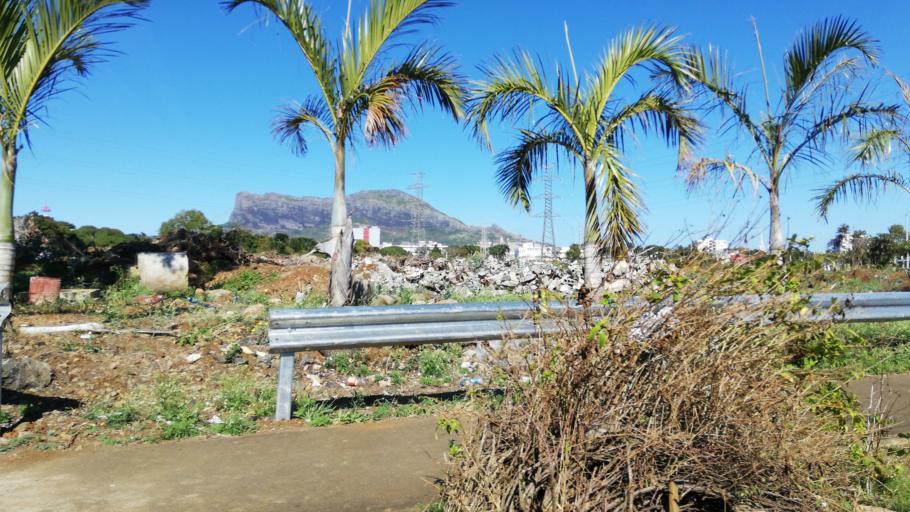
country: MU
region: Plaines Wilhems
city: Ebene
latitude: -20.2394
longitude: 57.4805
